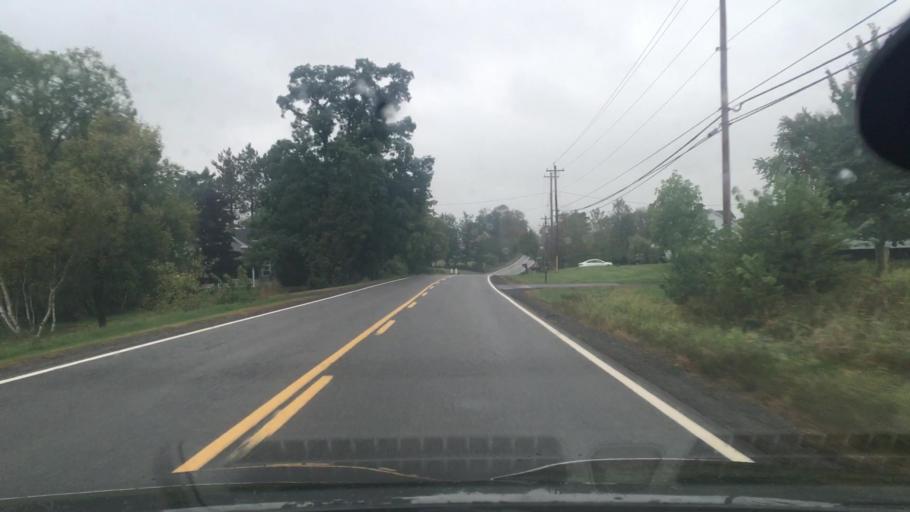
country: CA
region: Nova Scotia
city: Windsor
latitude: 44.9479
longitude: -64.1767
